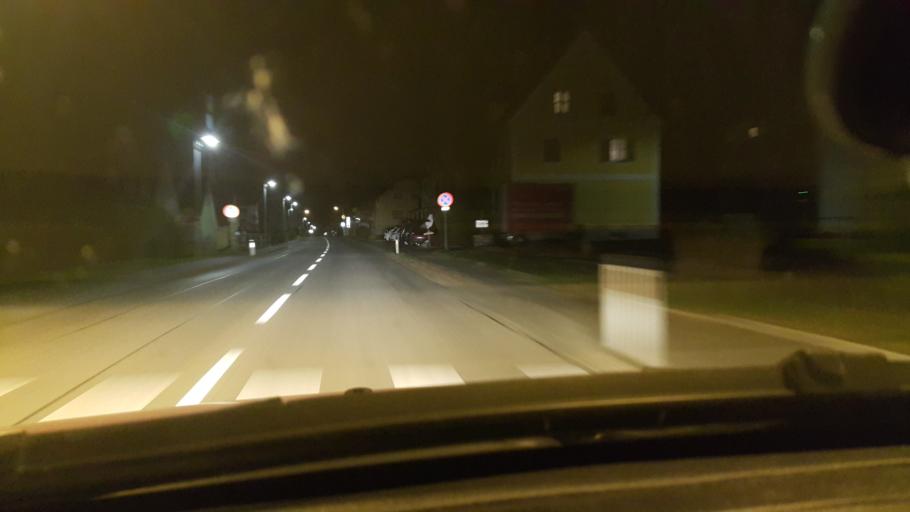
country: AT
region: Styria
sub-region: Politischer Bezirk Deutschlandsberg
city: Sankt Martin im Sulmtal
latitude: 46.7316
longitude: 15.3019
